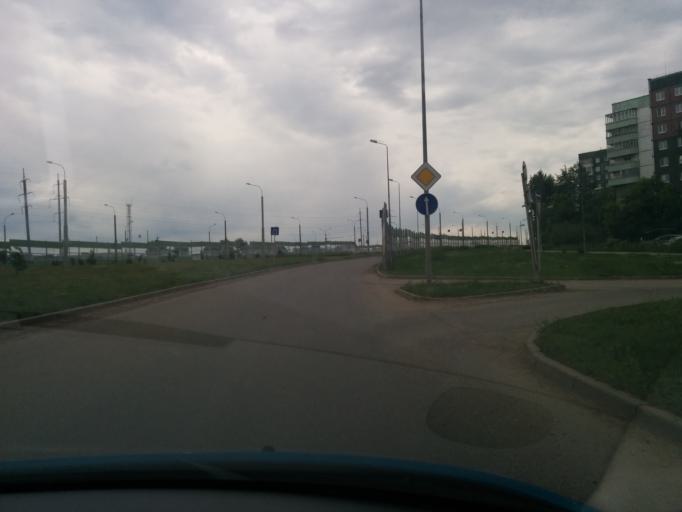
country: RU
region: Perm
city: Perm
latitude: 58.0012
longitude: 56.3135
